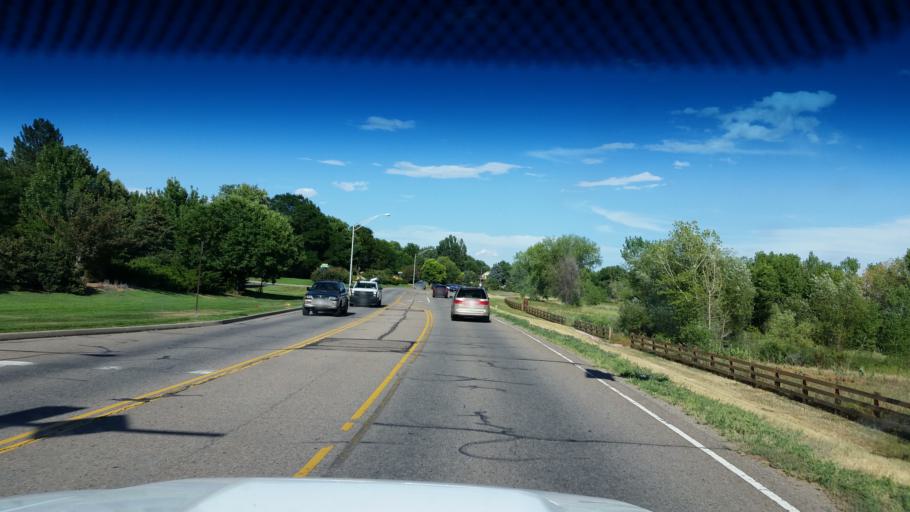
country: US
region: Colorado
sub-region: Adams County
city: Northglenn
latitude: 39.9286
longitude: -104.9544
